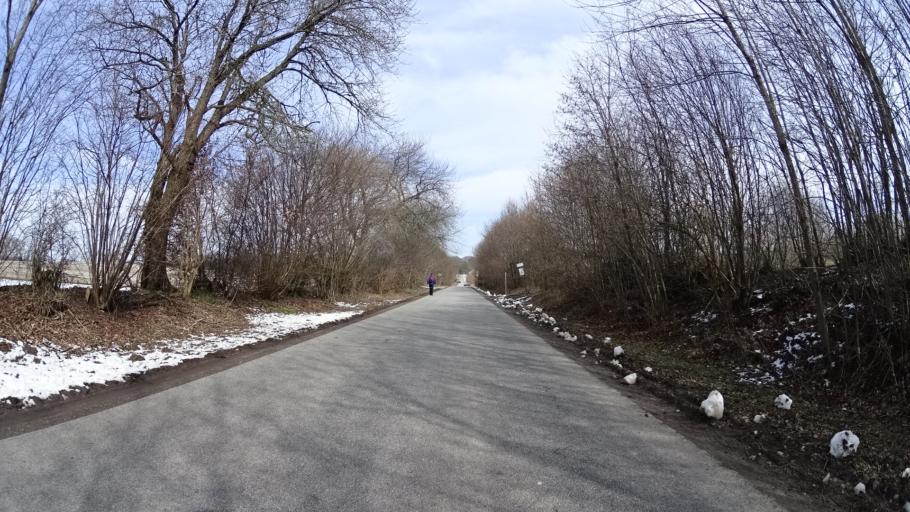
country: DE
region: Schleswig-Holstein
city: Stolpe
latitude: 54.1354
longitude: 10.2233
